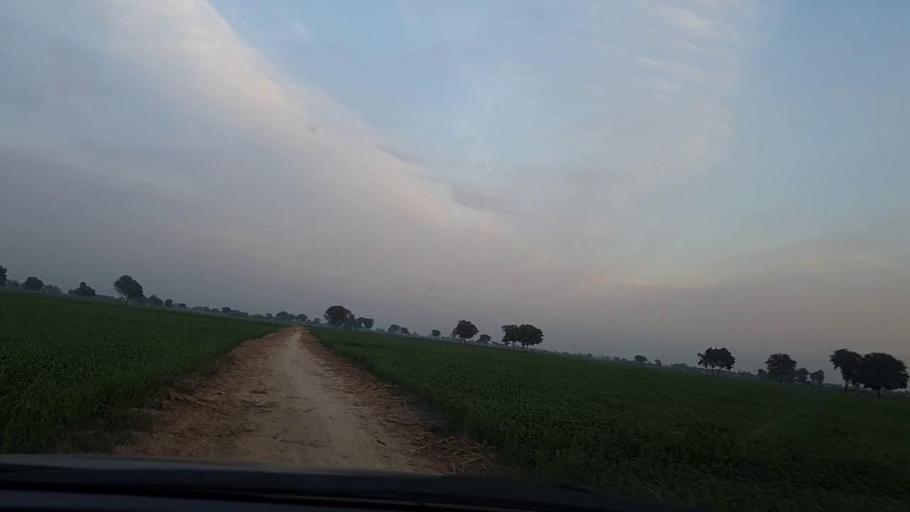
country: PK
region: Sindh
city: Sakrand
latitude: 26.1981
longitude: 68.3185
